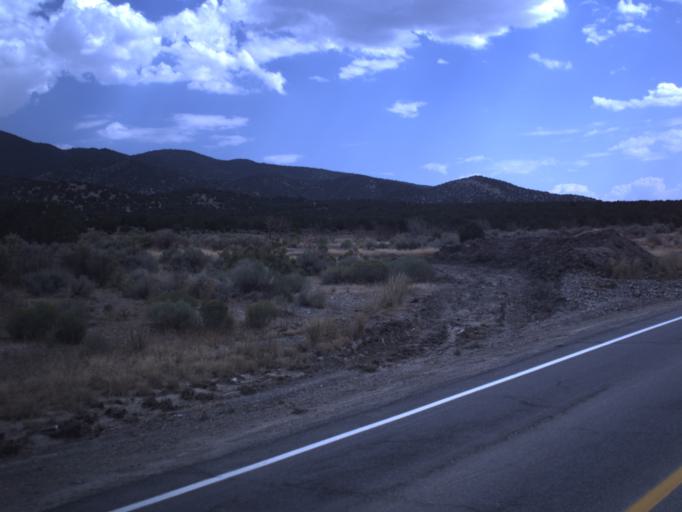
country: US
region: Utah
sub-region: Tooele County
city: Tooele
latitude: 40.3432
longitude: -112.3047
